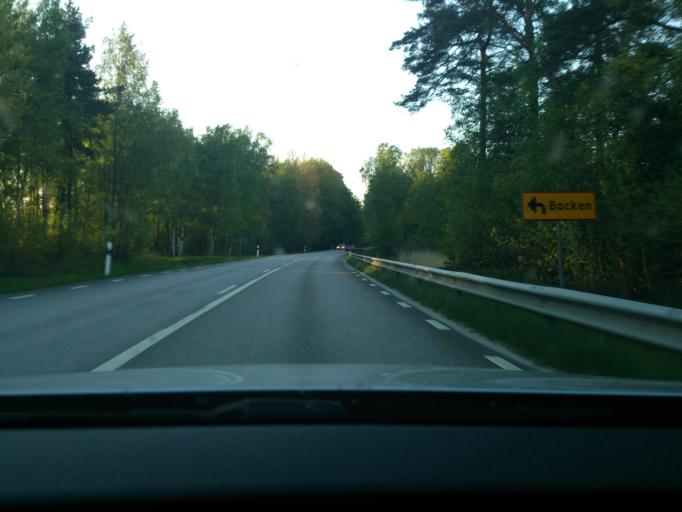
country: SE
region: Kronoberg
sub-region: Vaxjo Kommun
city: Gemla
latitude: 56.9646
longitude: 14.7117
